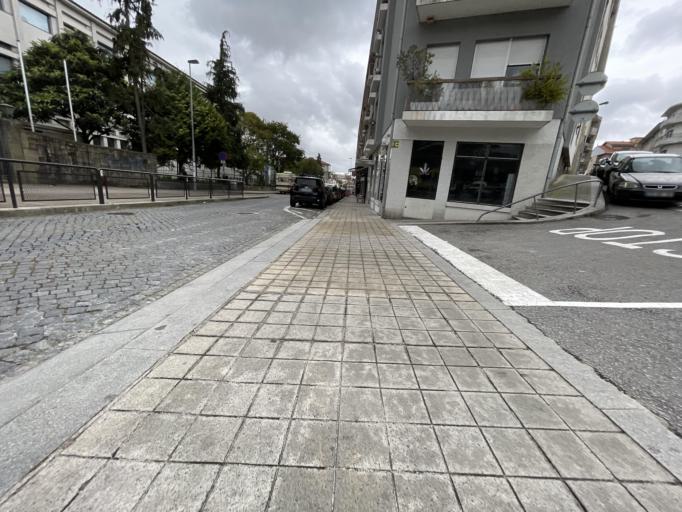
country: PT
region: Porto
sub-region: Porto
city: Porto
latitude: 41.1666
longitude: -8.6077
